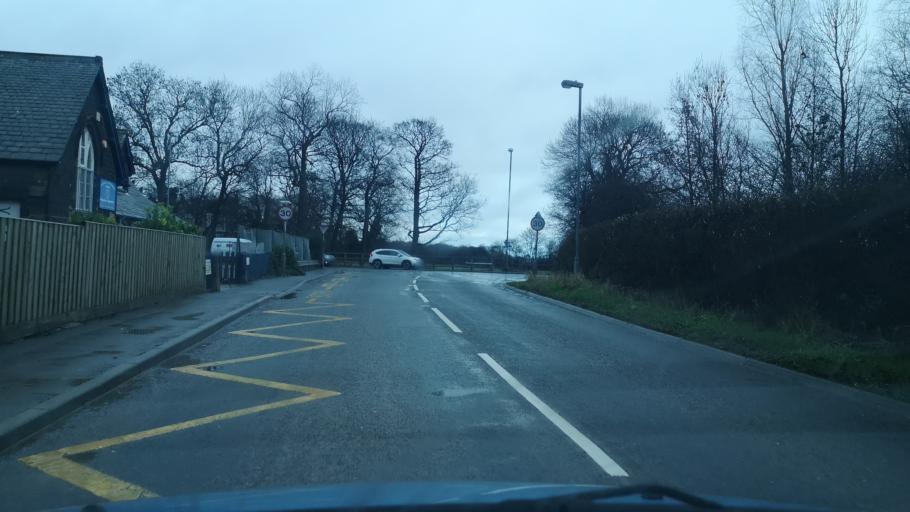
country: GB
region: England
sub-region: City and Borough of Wakefield
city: Fitzwilliam
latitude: 53.6471
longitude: -1.3873
